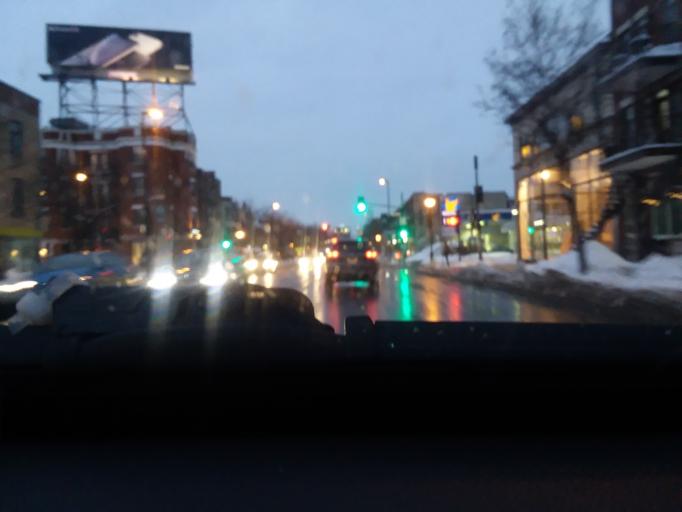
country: CA
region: Quebec
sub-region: Montreal
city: Montreal
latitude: 45.5183
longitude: -73.5930
